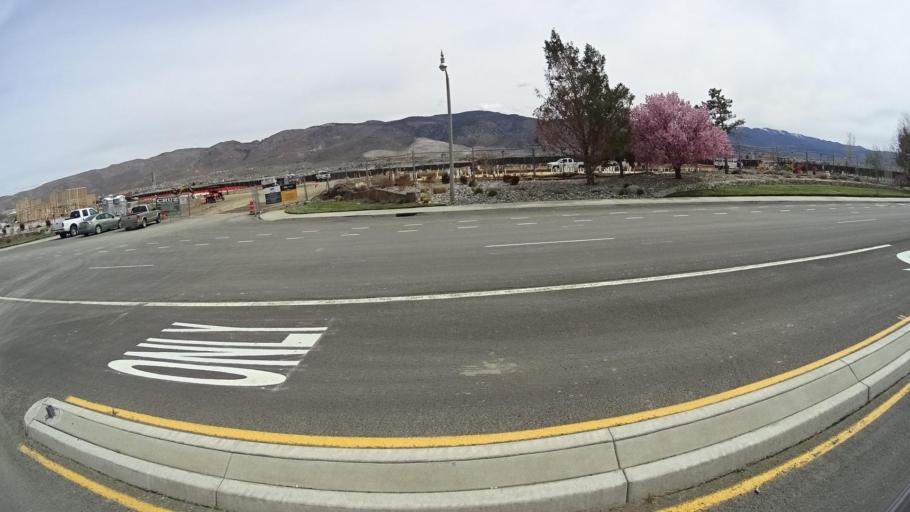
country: US
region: Nevada
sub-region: Washoe County
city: Sparks
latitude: 39.4200
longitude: -119.7415
